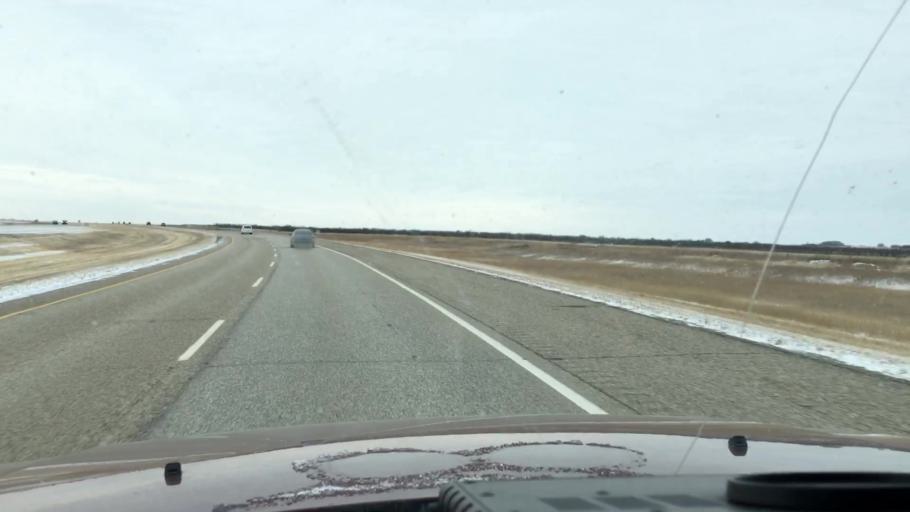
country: CA
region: Saskatchewan
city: Saskatoon
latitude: 51.4716
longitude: -106.2480
